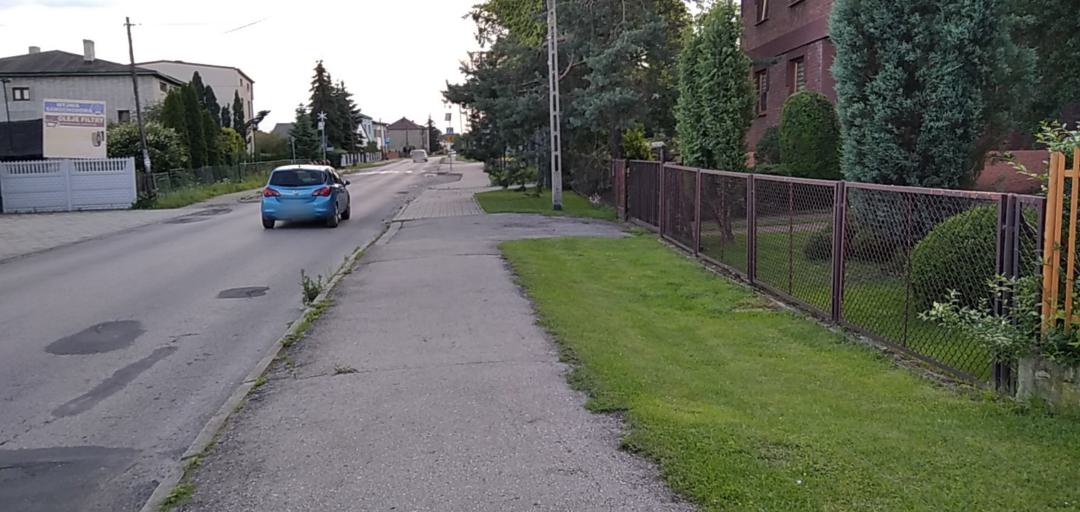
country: PL
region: Silesian Voivodeship
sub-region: Powiat bedzinski
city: Psary
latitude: 50.4055
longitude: 19.1375
